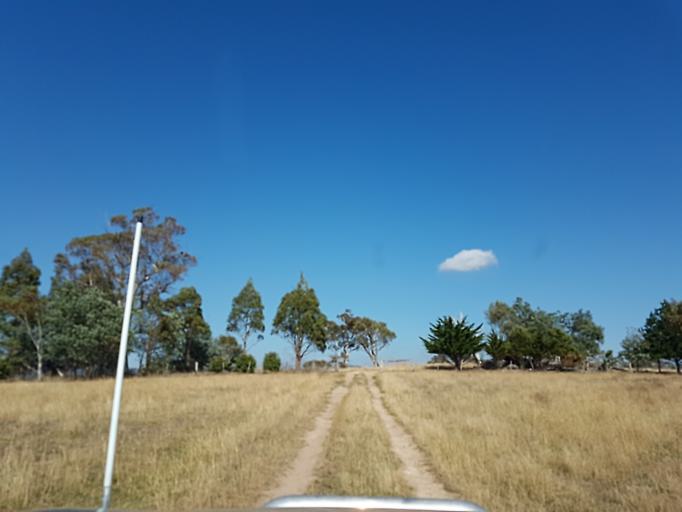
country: AU
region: New South Wales
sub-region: Snowy River
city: Jindabyne
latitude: -37.0487
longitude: 148.2904
